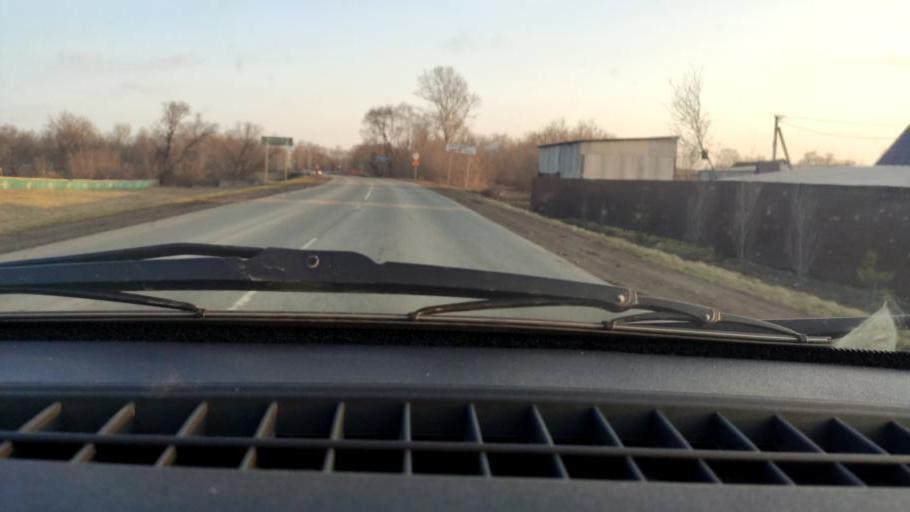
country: RU
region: Bashkortostan
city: Davlekanovo
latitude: 54.3673
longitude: 55.1955
